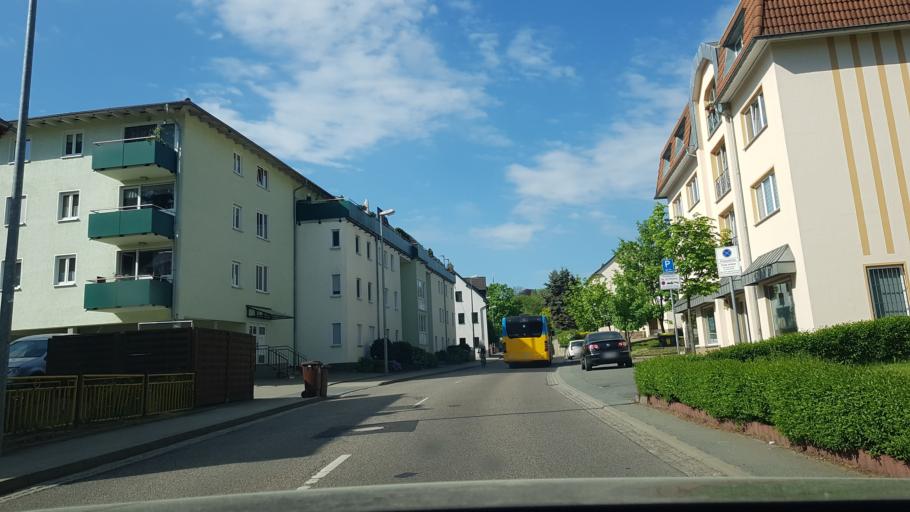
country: DE
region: Saxony
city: Wittgensdorf
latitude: 50.8833
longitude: 12.8717
